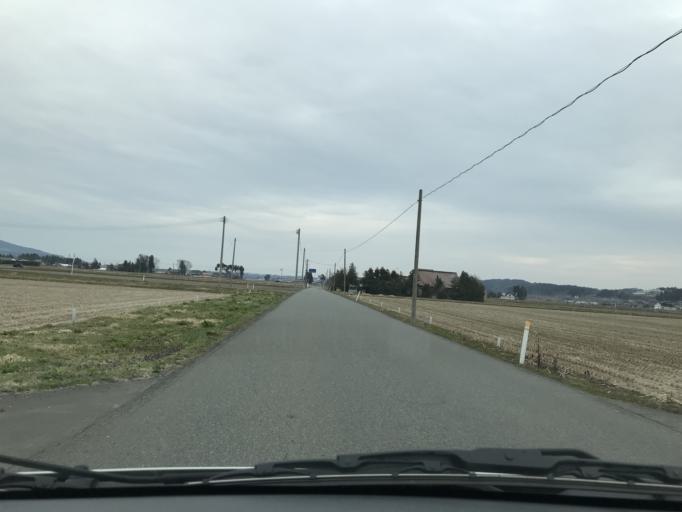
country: JP
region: Iwate
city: Mizusawa
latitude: 39.0794
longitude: 141.1429
